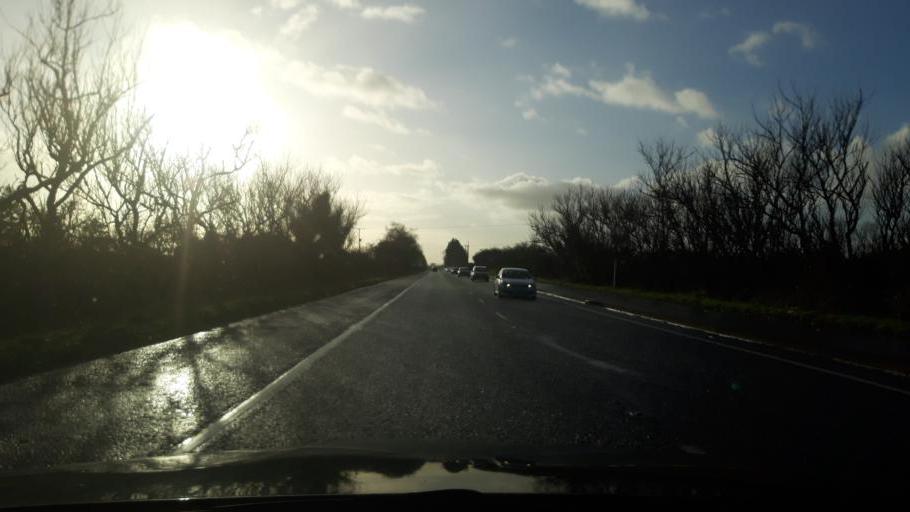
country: GB
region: Northern Ireland
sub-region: Coleraine District
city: Coleraine
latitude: 55.1133
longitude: -6.6880
